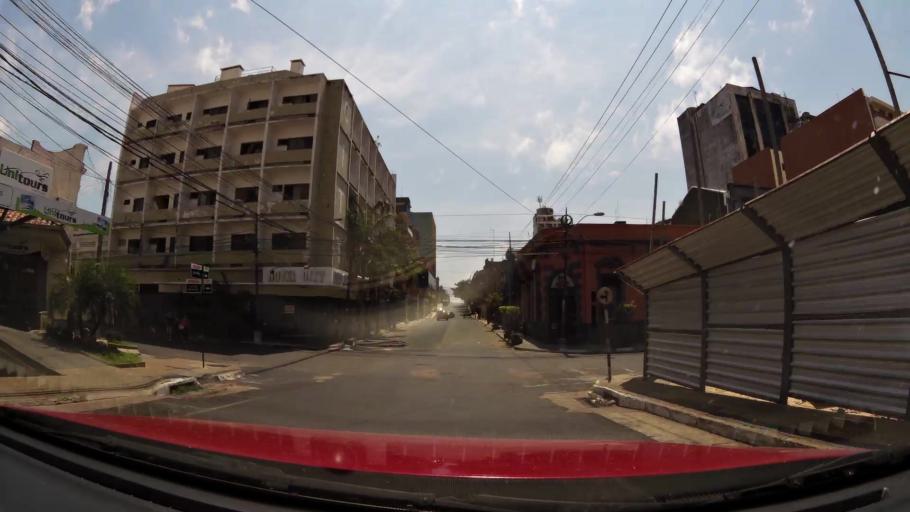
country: PY
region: Asuncion
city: Asuncion
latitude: -25.2861
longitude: -57.6369
